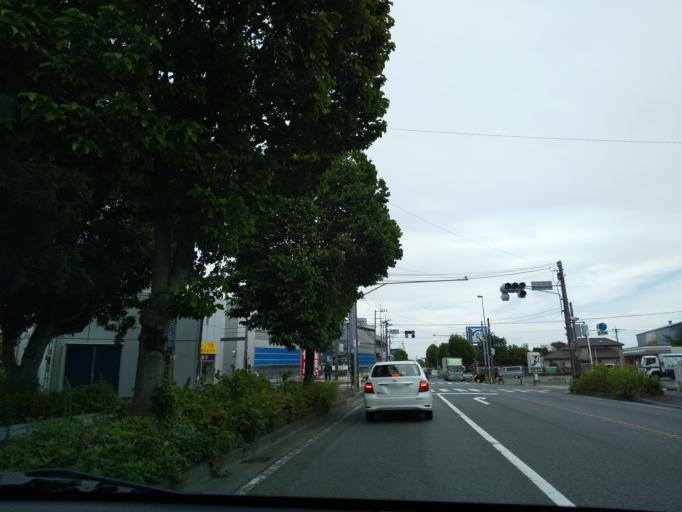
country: JP
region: Kanagawa
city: Zama
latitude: 35.5271
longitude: 139.3976
